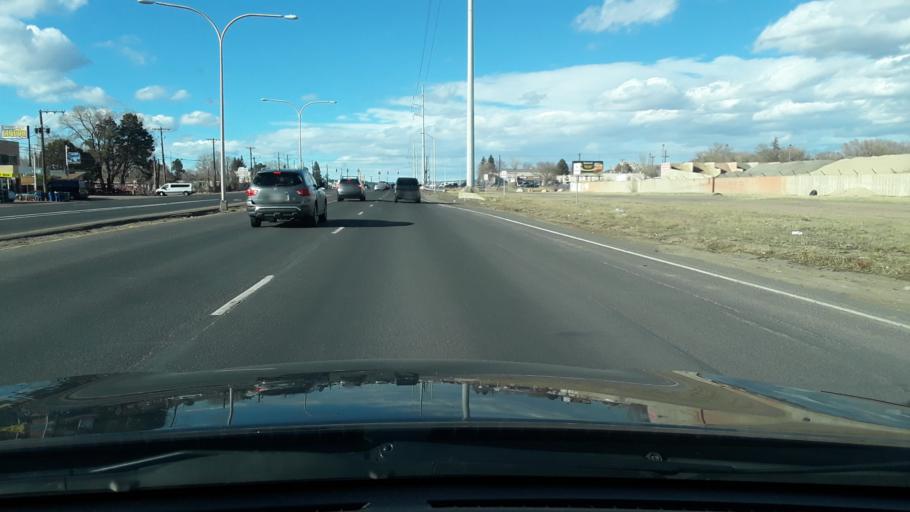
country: US
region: Colorado
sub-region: El Paso County
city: Colorado Springs
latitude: 38.8872
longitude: -104.8189
